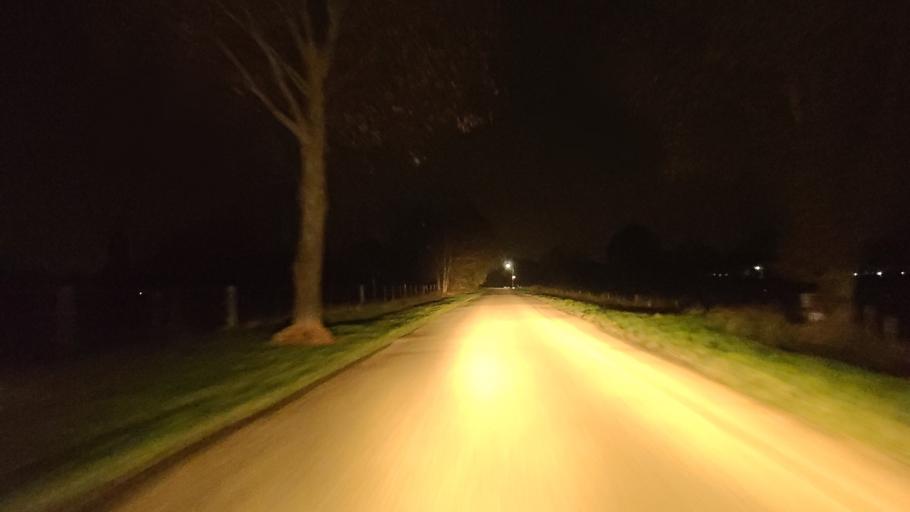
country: NL
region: Limburg
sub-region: Gemeente Gennep
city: Gennep
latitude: 51.7205
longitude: 5.9682
